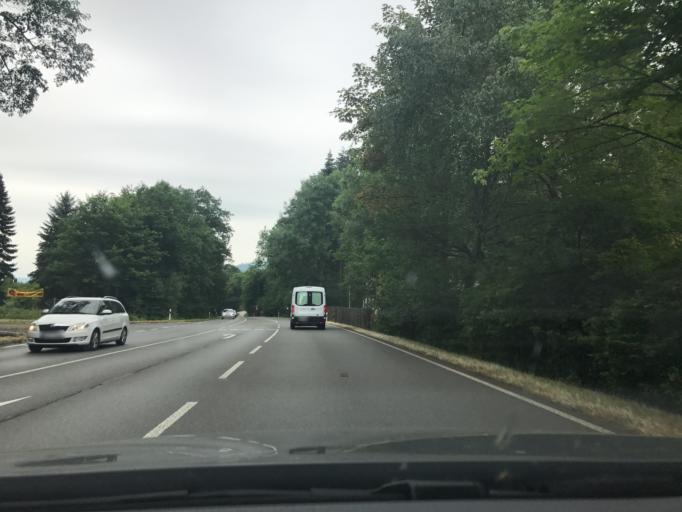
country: DE
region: Hesse
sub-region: Regierungsbezirk Kassel
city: Baunatal
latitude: 51.2762
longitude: 9.3999
